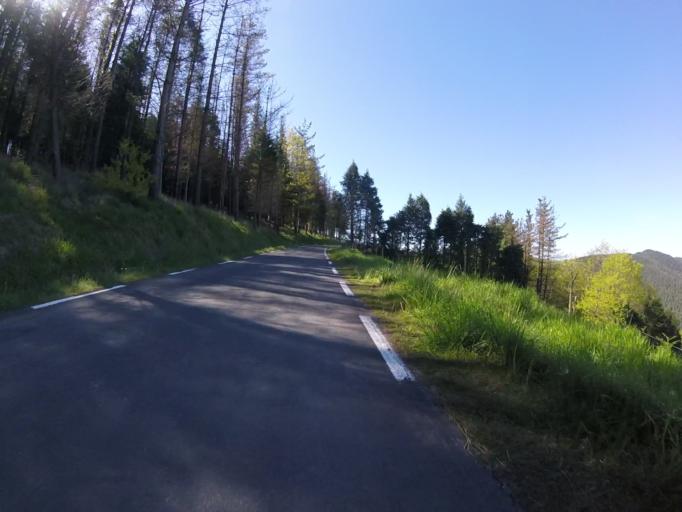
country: ES
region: Basque Country
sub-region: Provincia de Guipuzcoa
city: Errezil
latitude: 43.2106
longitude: -2.2011
